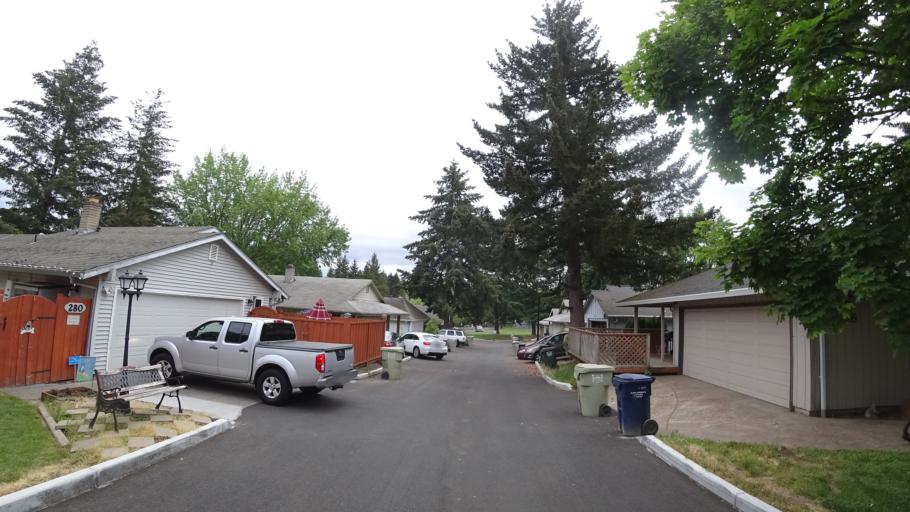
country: US
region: Oregon
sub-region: Washington County
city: Aloha
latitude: 45.5220
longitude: -122.8635
